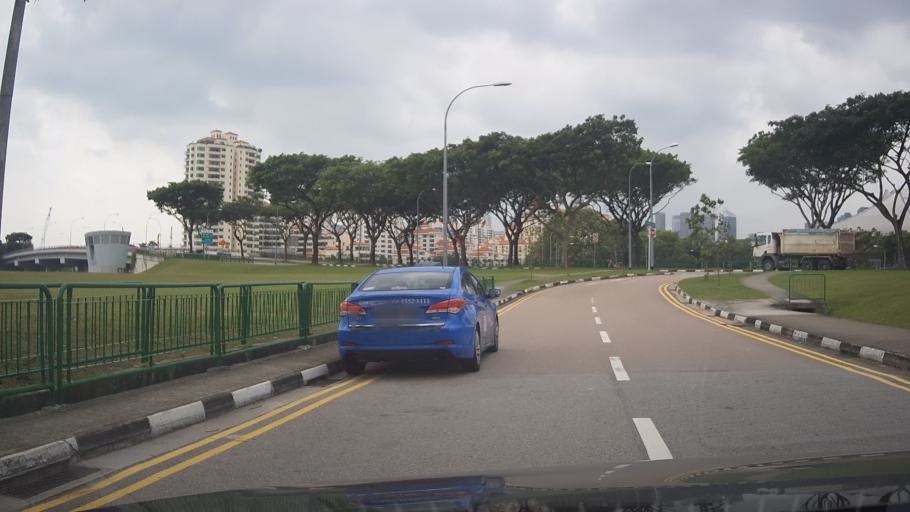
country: SG
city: Singapore
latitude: 1.3006
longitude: 103.8787
